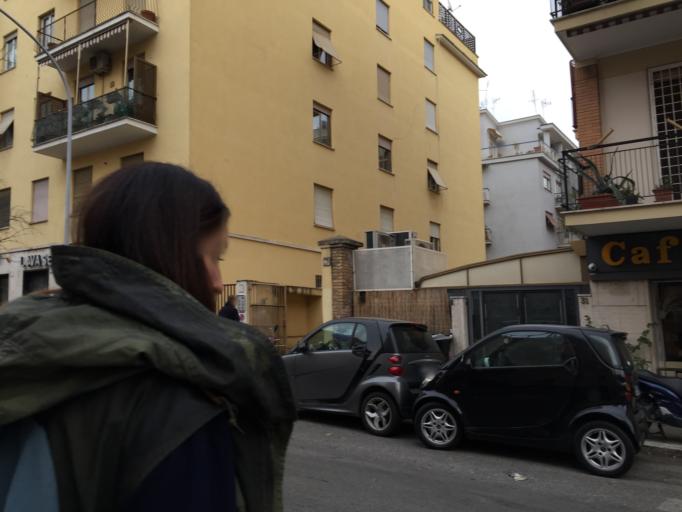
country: VA
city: Vatican City
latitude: 41.8819
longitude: 12.4568
